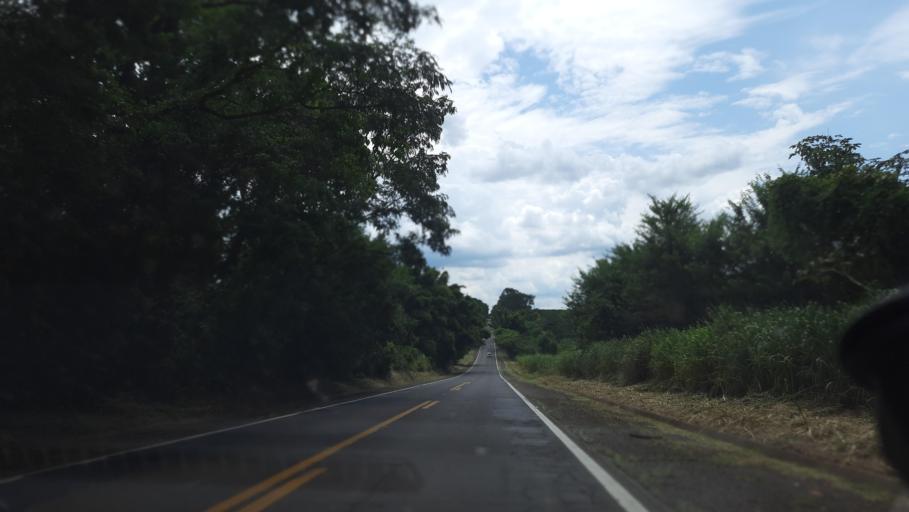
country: BR
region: Sao Paulo
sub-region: Mococa
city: Mococa
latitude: -21.5016
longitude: -47.0584
